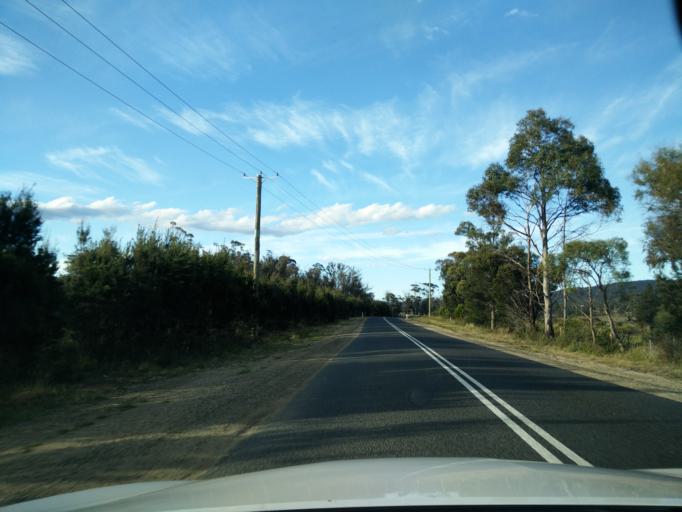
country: AU
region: Tasmania
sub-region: Break O'Day
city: St Helens
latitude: -41.8990
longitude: 148.2550
